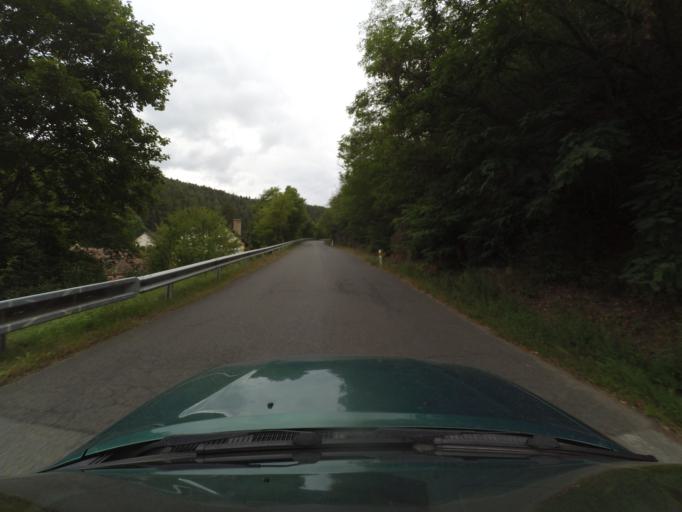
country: CZ
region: Plzensky
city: Kralovice
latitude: 49.9161
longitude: 13.5186
